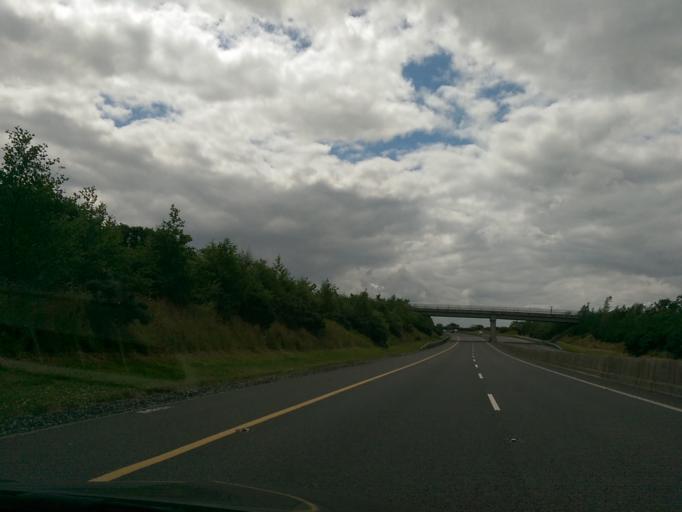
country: IE
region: Munster
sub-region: County Cork
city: Mitchelstown
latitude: 52.2486
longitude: -8.2640
